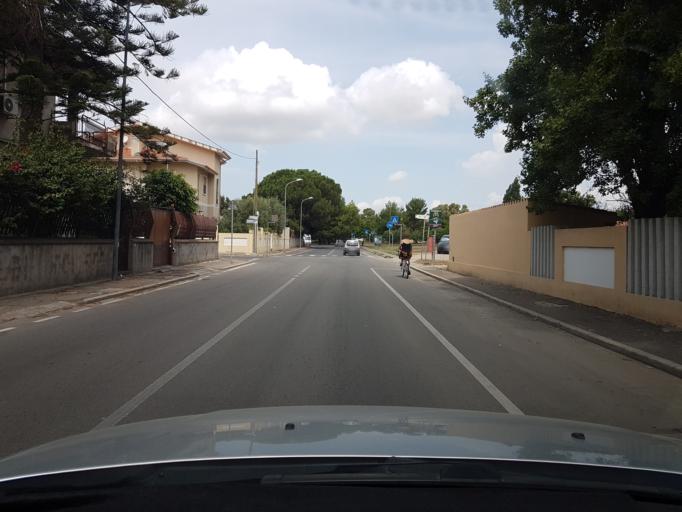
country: IT
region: Sardinia
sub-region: Provincia di Oristano
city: Oristano
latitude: 39.9119
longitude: 8.5902
